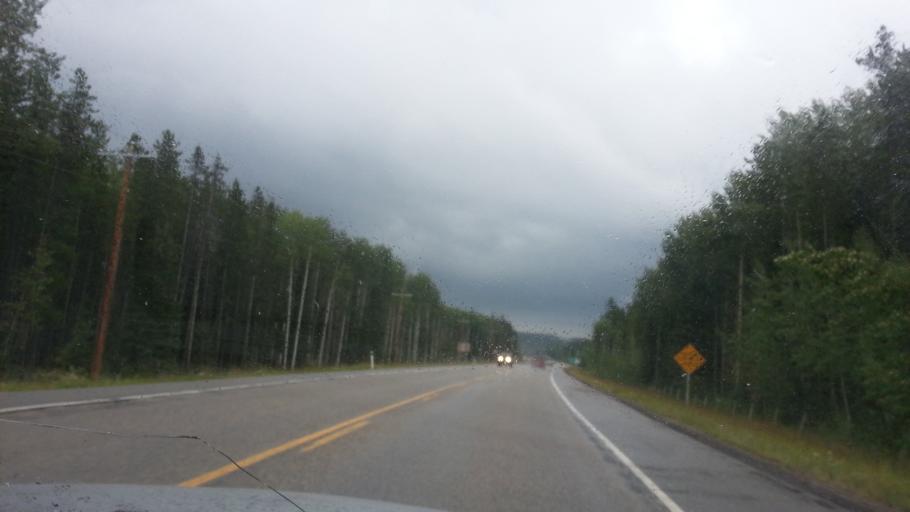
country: CA
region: Alberta
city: Cochrane
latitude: 50.9219
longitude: -114.5680
